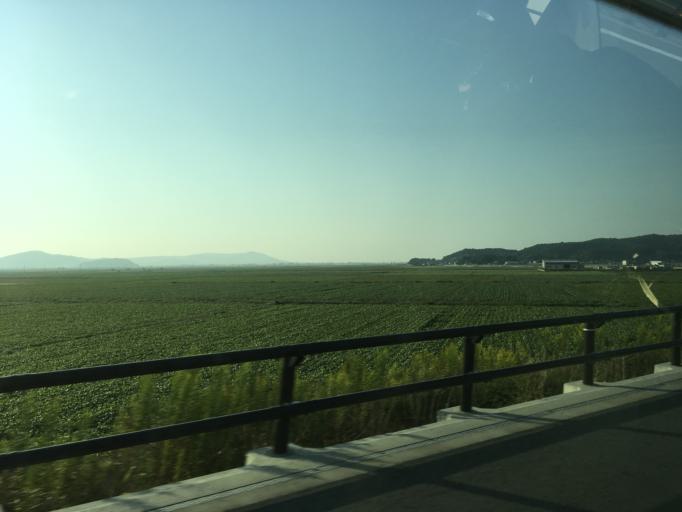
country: JP
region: Miyagi
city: Ishinomaki
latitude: 38.5165
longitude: 141.2884
